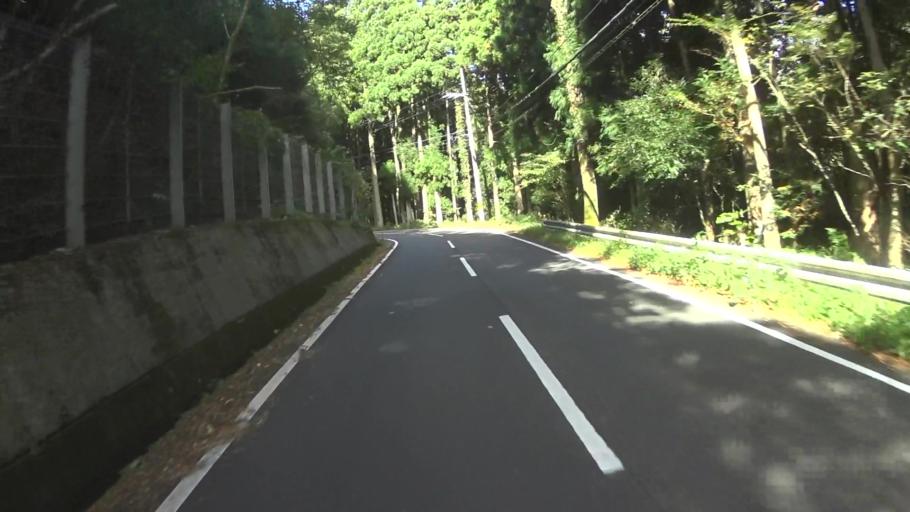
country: JP
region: Kyoto
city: Maizuru
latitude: 35.5332
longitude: 135.4419
